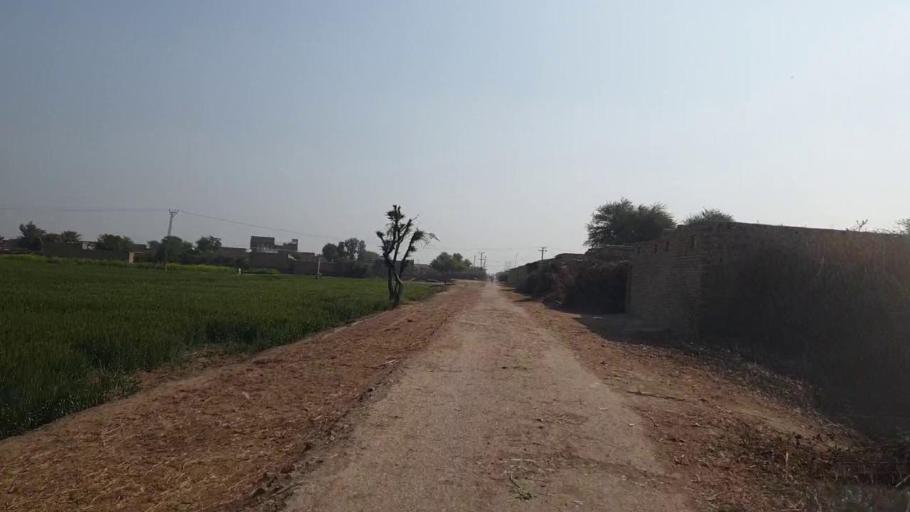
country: PK
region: Sindh
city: Bhit Shah
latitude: 25.7295
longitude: 68.5317
